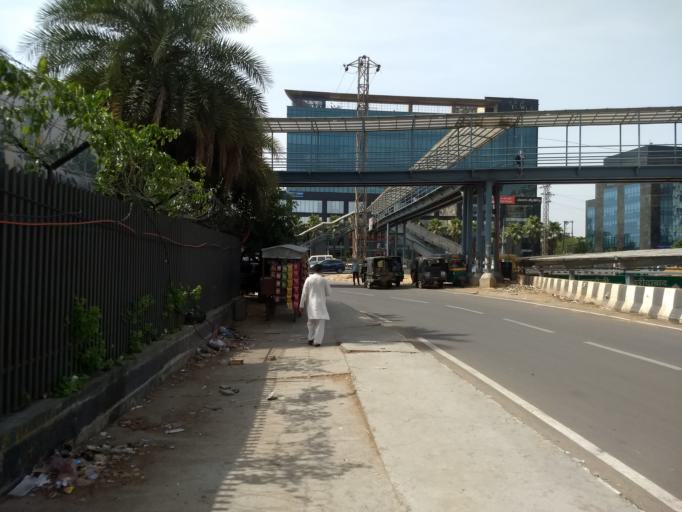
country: IN
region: Haryana
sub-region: Gurgaon
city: Gurgaon
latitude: 28.4774
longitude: 77.0713
